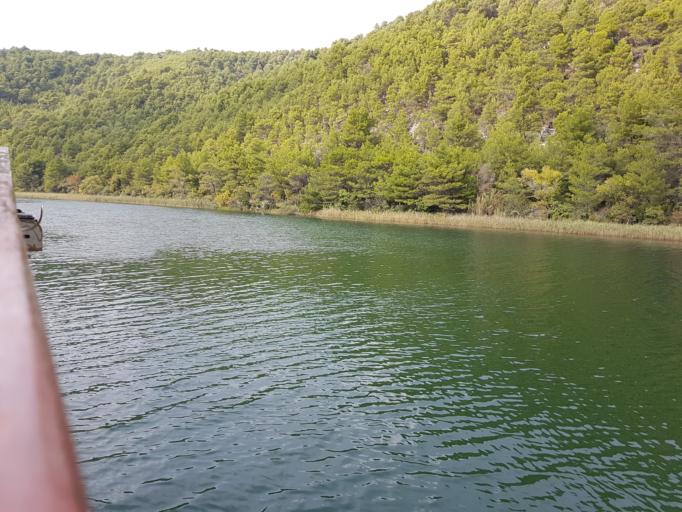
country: HR
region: Sibensko-Kniniska
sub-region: Grad Sibenik
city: Sibenik
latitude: 43.8206
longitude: 15.9466
